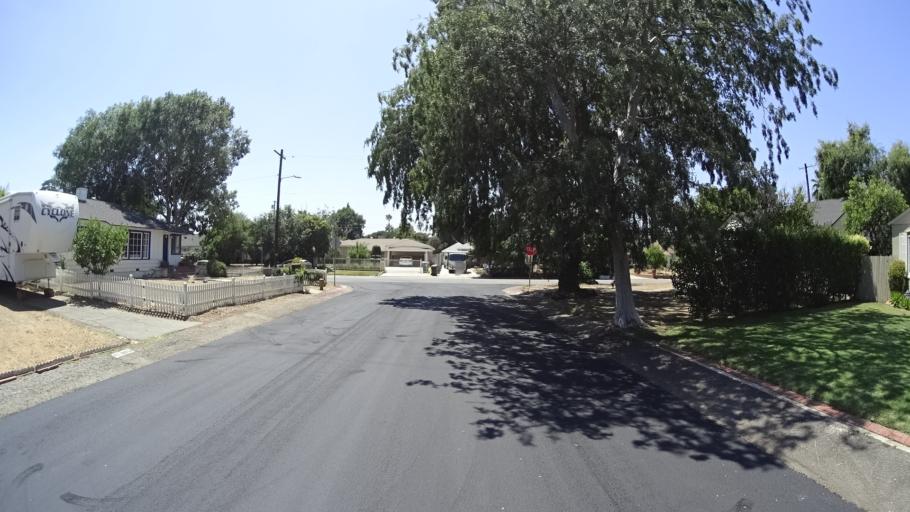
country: US
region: California
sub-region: Los Angeles County
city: Van Nuys
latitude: 34.1894
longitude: -118.4352
